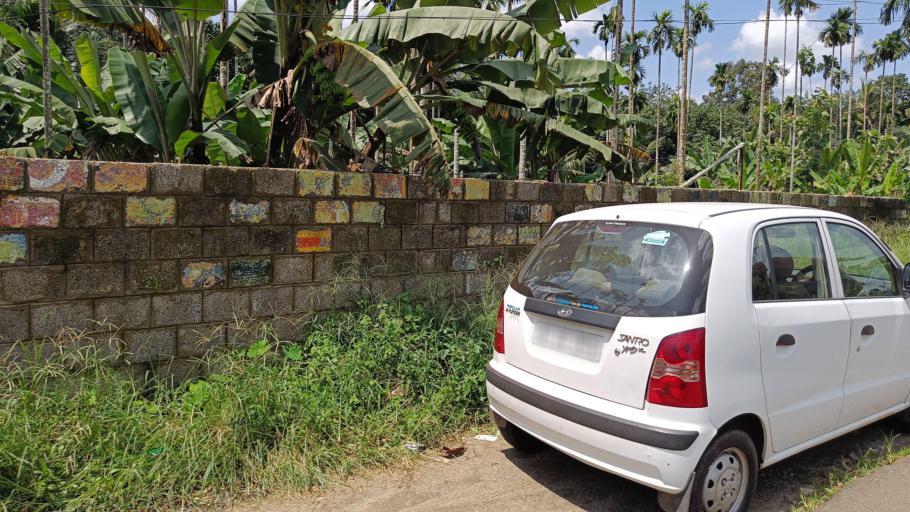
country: IN
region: Kerala
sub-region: Kottayam
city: Erattupetta
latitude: 9.5602
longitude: 76.8118
